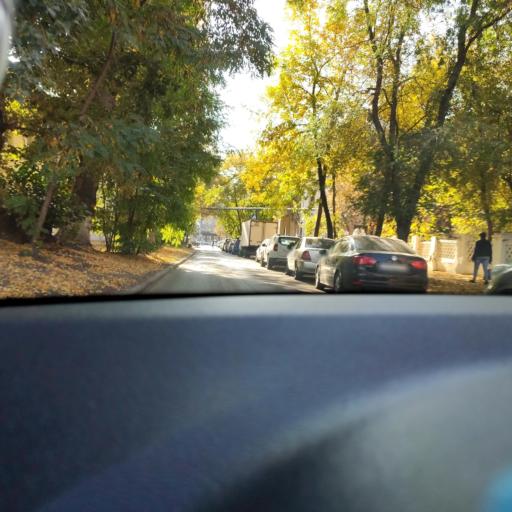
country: RU
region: Samara
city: Samara
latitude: 53.1960
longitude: 50.1314
